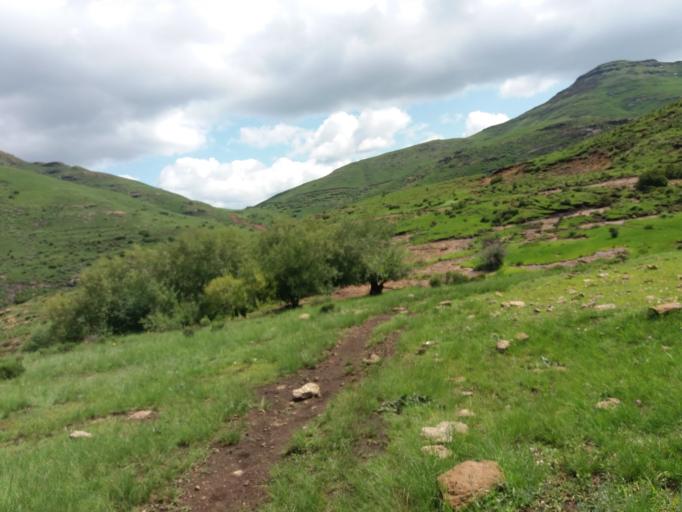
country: LS
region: Maseru
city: Nako
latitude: -29.6751
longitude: 27.9111
